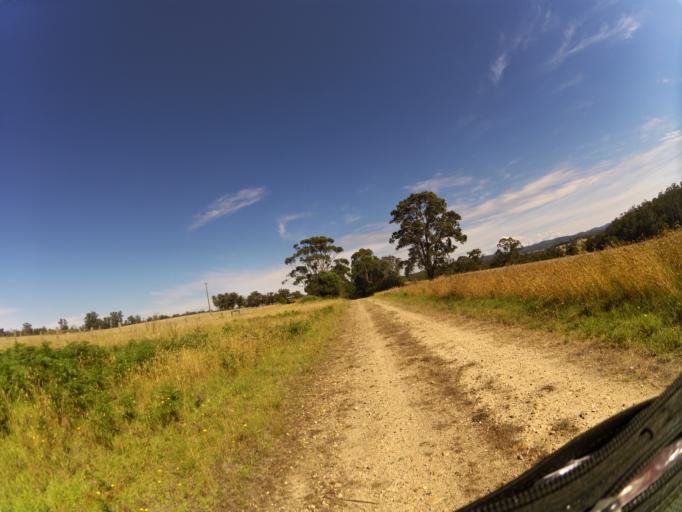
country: AU
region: Victoria
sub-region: East Gippsland
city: Lakes Entrance
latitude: -37.7382
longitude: 148.1681
